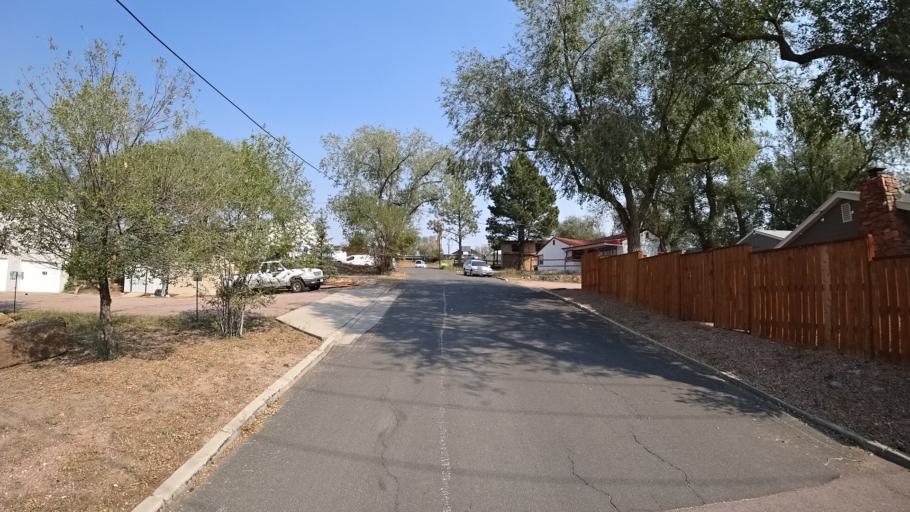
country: US
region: Colorado
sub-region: El Paso County
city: Colorado Springs
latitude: 38.8129
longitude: -104.8398
